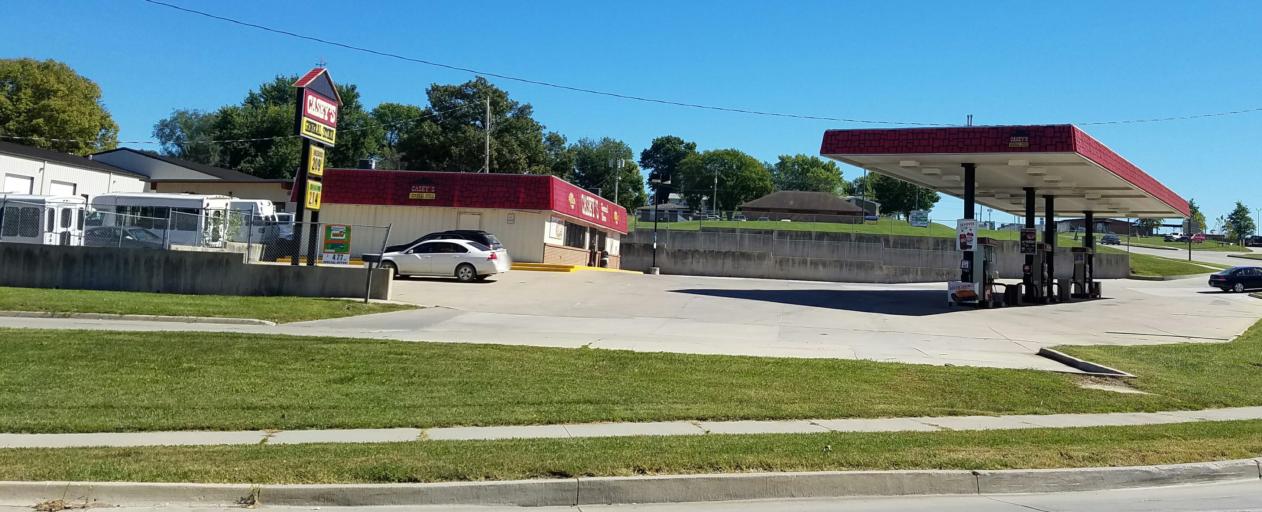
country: US
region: Missouri
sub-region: Harrison County
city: Bethany
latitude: 40.2656
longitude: -94.0270
